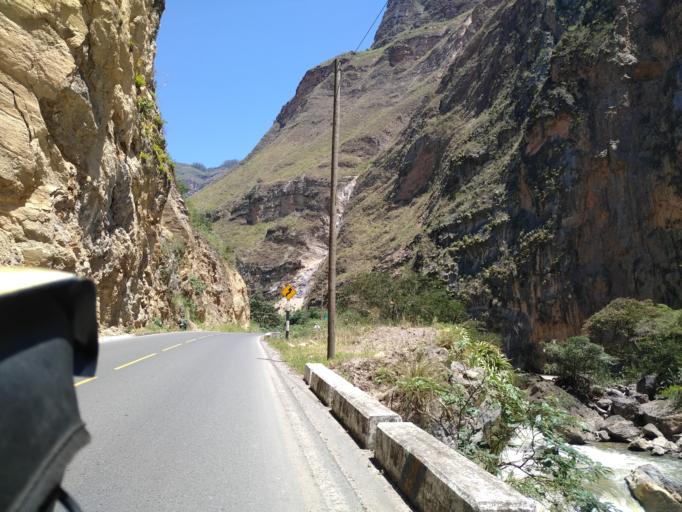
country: PE
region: Amazonas
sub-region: Provincia de Luya
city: Olto
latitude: -6.0745
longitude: -77.9097
